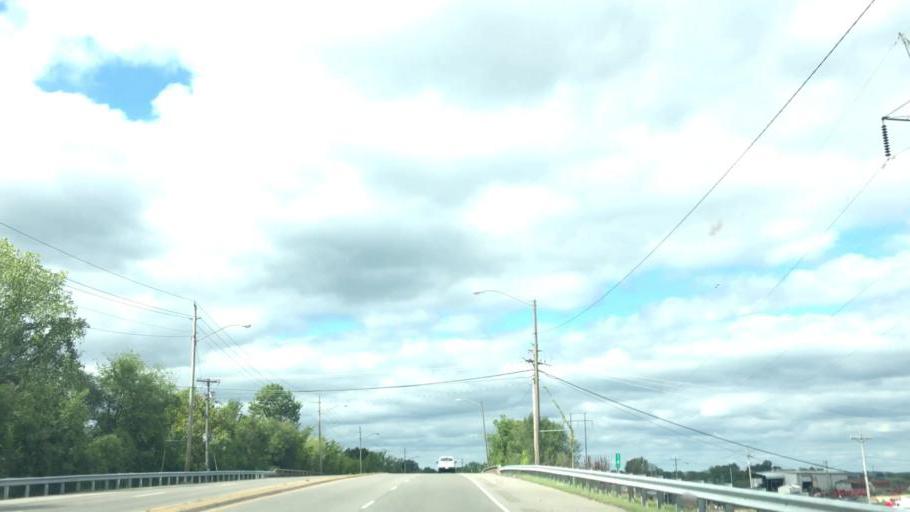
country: US
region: Tennessee
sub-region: Maury County
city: Columbia
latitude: 35.6082
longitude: -87.0693
